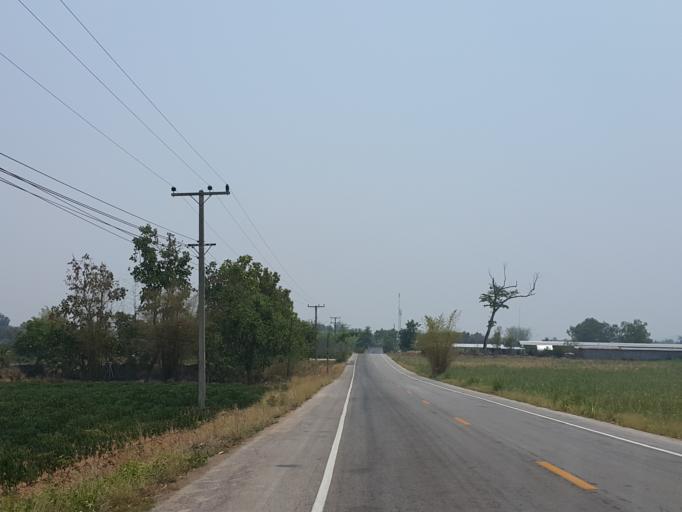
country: TH
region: Kamphaeng Phet
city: Pang Sila Thong
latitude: 16.0399
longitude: 99.3746
